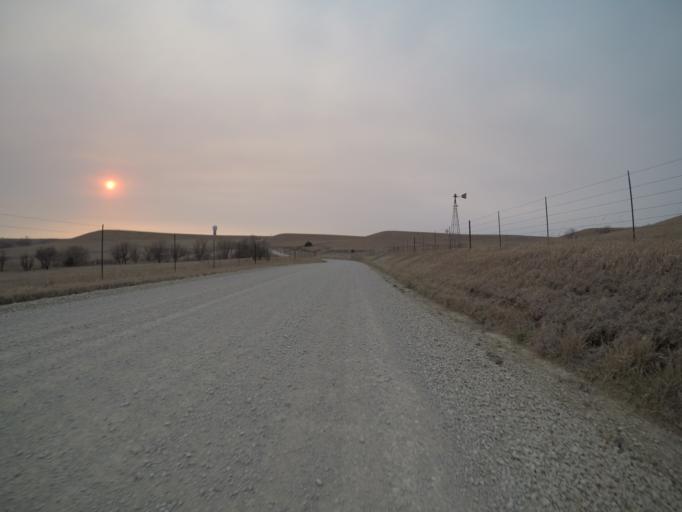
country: US
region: Kansas
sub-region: Riley County
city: Manhattan
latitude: 39.2265
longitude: -96.6362
